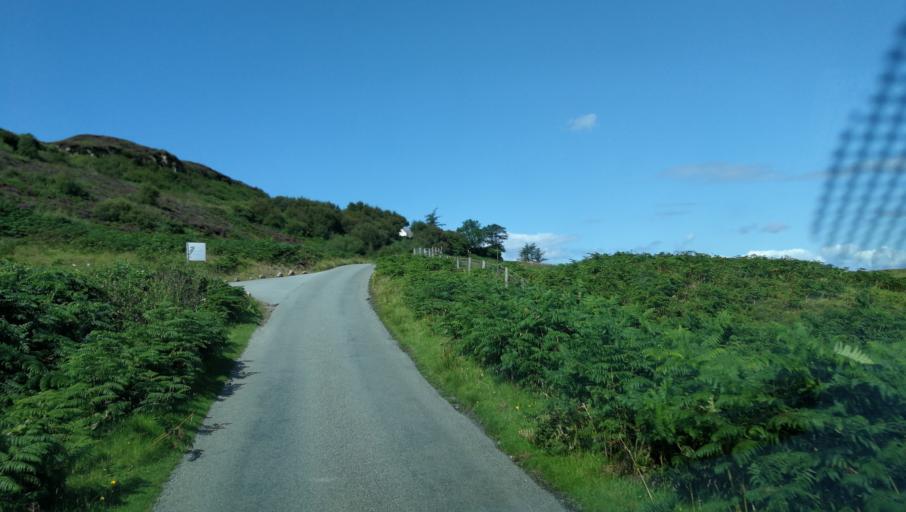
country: GB
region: Scotland
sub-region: Highland
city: Isle of Skye
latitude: 57.4500
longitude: -6.6540
